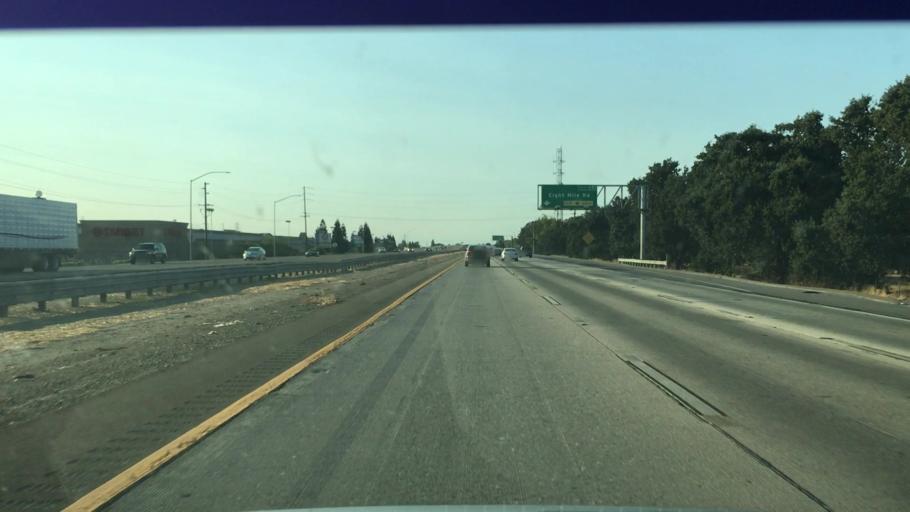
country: US
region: California
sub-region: San Joaquin County
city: Lincoln Village
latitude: 38.0503
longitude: -121.3702
